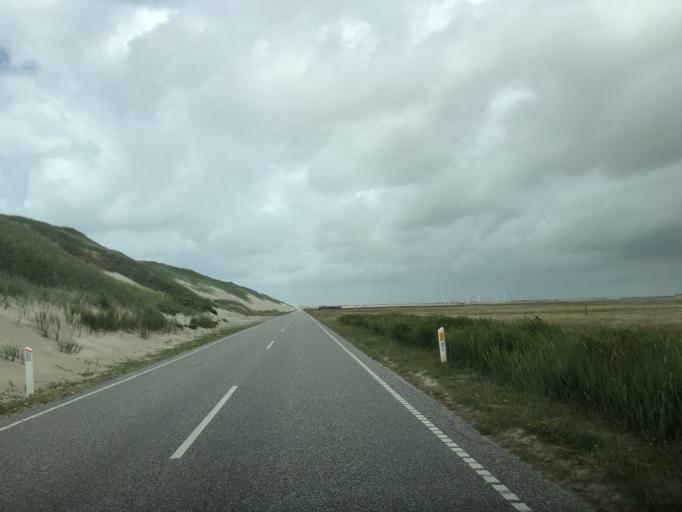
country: DK
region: Central Jutland
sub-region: Lemvig Kommune
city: Harboore
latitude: 56.4367
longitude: 8.1245
